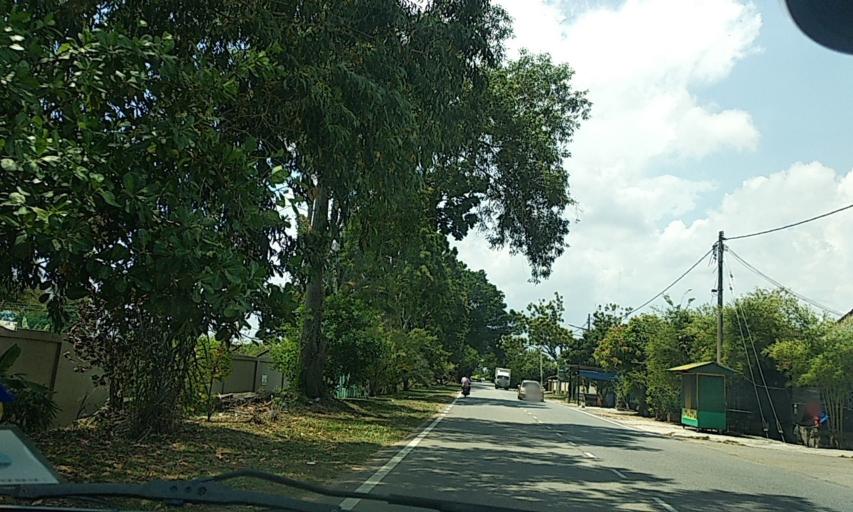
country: MY
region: Kedah
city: Sungai Petani
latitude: 5.6339
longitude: 100.4677
